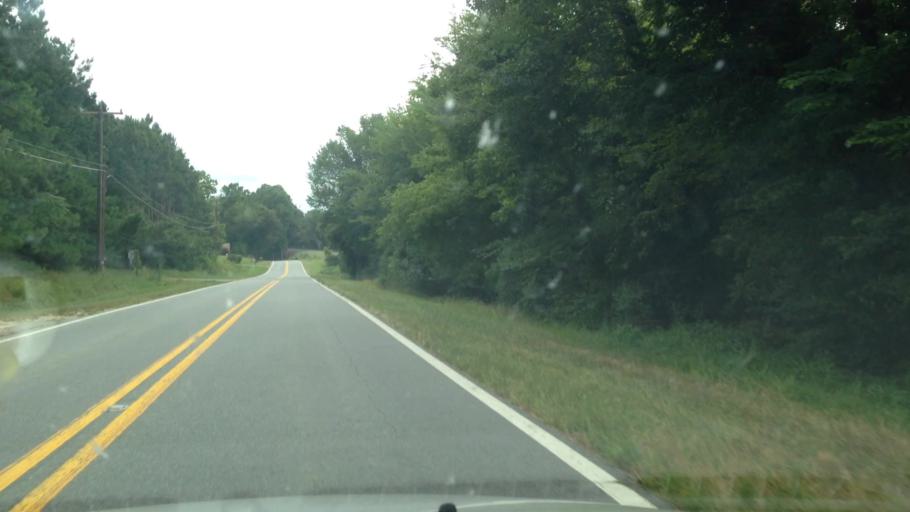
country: US
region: North Carolina
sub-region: Rockingham County
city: Reidsville
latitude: 36.4152
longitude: -79.6031
